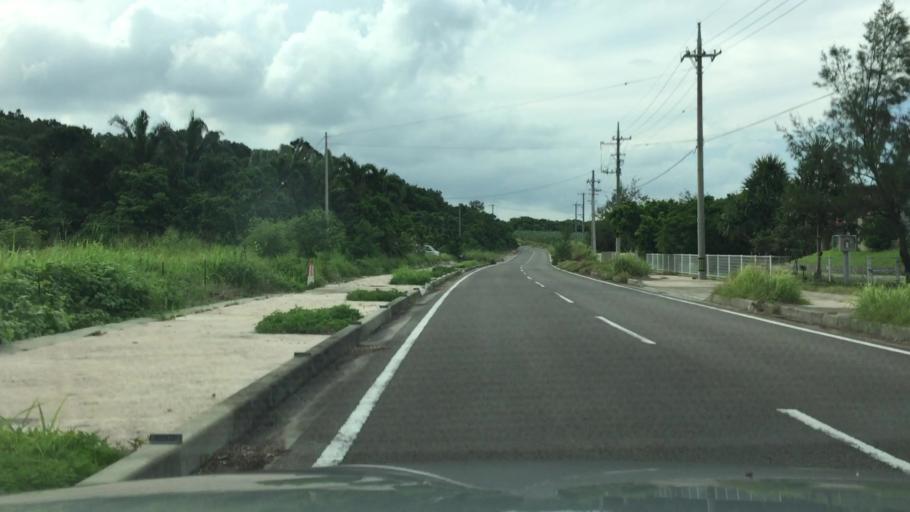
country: JP
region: Okinawa
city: Ishigaki
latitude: 24.4664
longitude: 124.1413
